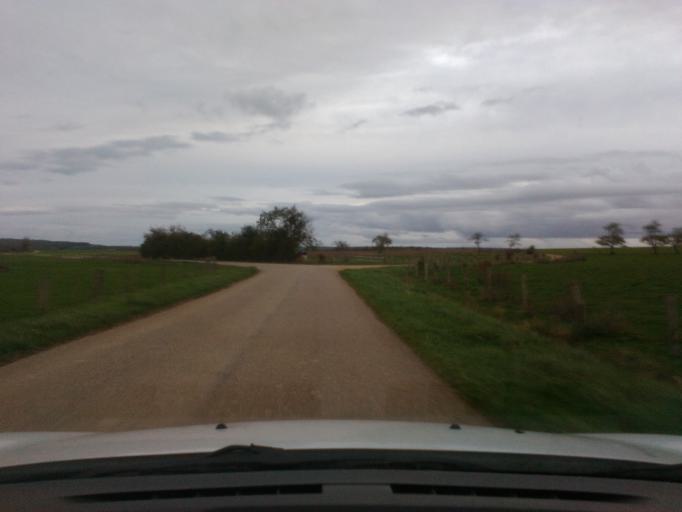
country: FR
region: Lorraine
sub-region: Departement des Vosges
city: Mirecourt
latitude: 48.3311
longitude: 6.0637
